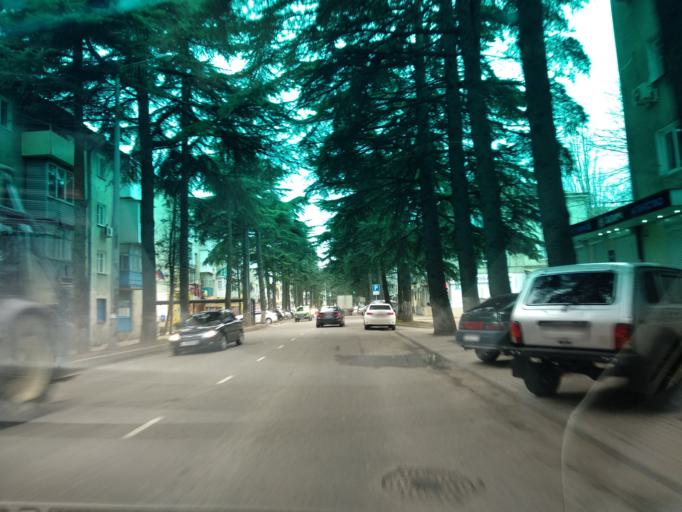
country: RU
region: Krasnodarskiy
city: Tuapse
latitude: 44.0991
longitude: 39.0826
